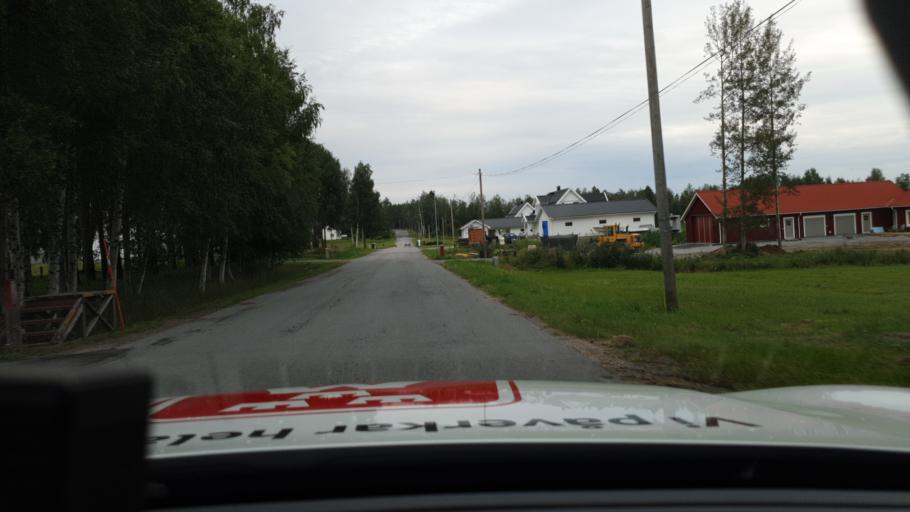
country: SE
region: Norrbotten
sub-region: Lulea Kommun
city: Sodra Sunderbyn
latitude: 65.6745
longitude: 21.8830
